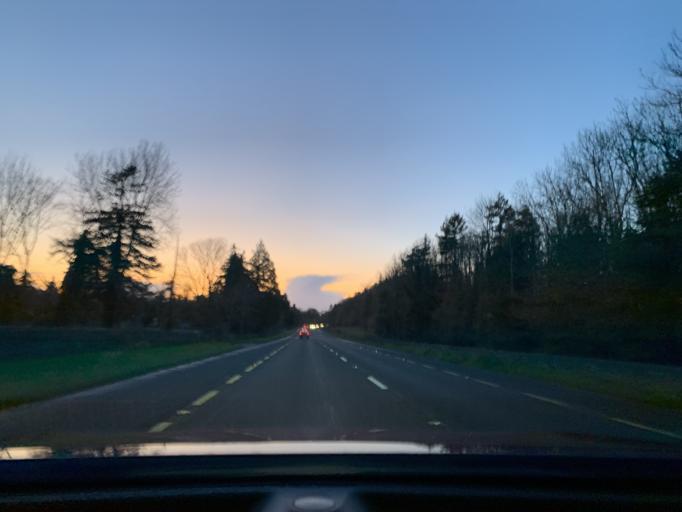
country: IE
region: Connaught
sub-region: Roscommon
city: Boyle
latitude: 53.9696
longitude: -8.2161
